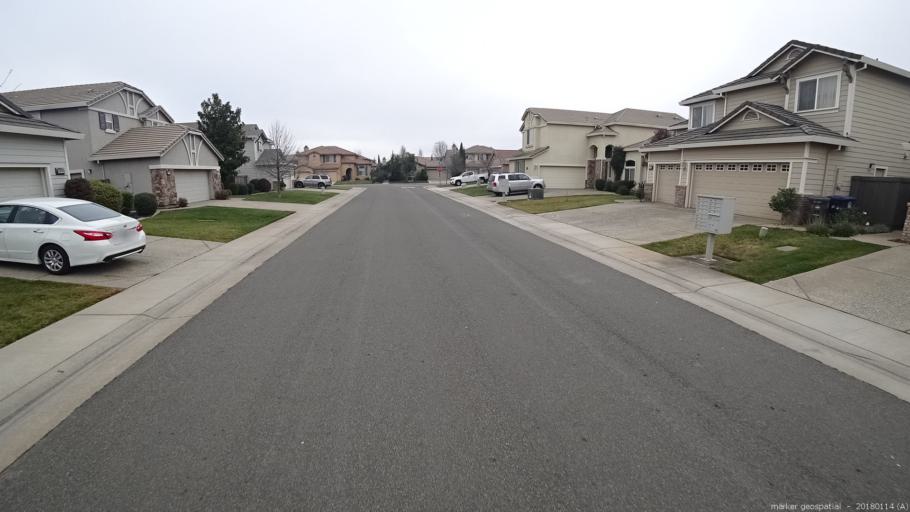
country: US
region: California
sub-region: Sacramento County
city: Gold River
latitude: 38.5465
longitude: -121.2331
